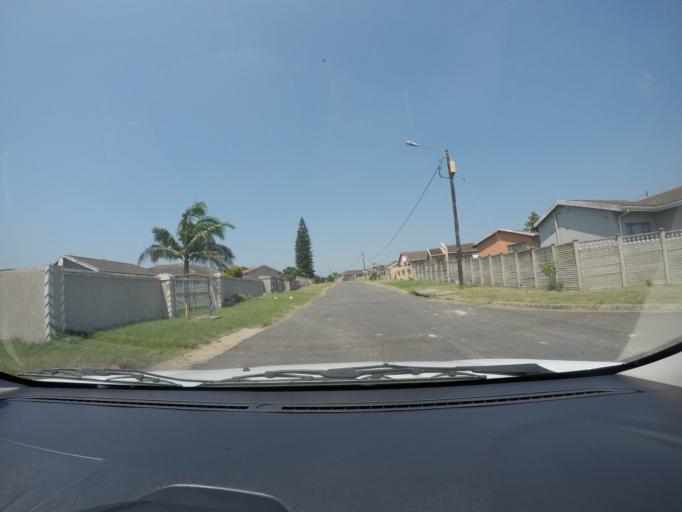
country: ZA
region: KwaZulu-Natal
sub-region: uThungulu District Municipality
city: eSikhawini
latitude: -28.8659
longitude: 31.9206
